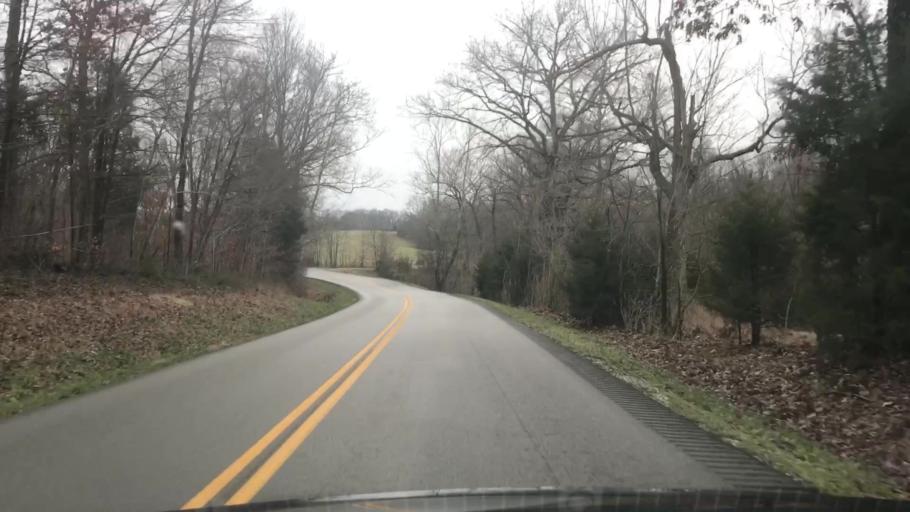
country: US
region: Kentucky
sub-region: Monroe County
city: Tompkinsville
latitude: 36.8484
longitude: -85.7694
